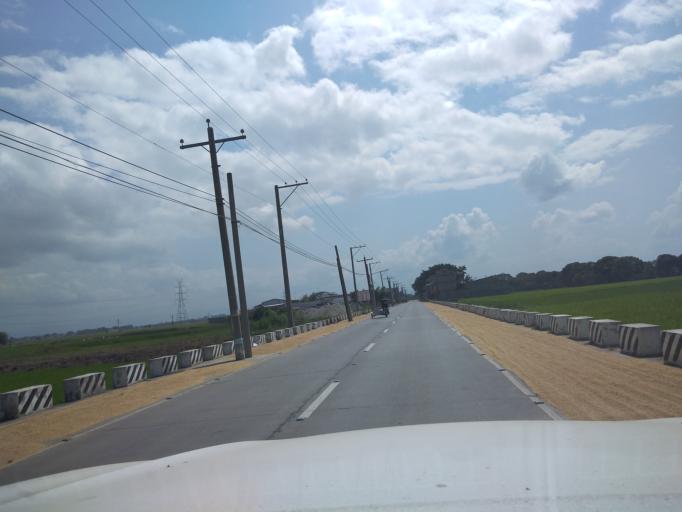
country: PH
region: Central Luzon
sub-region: Province of Pampanga
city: Talang
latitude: 15.0249
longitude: 120.8409
